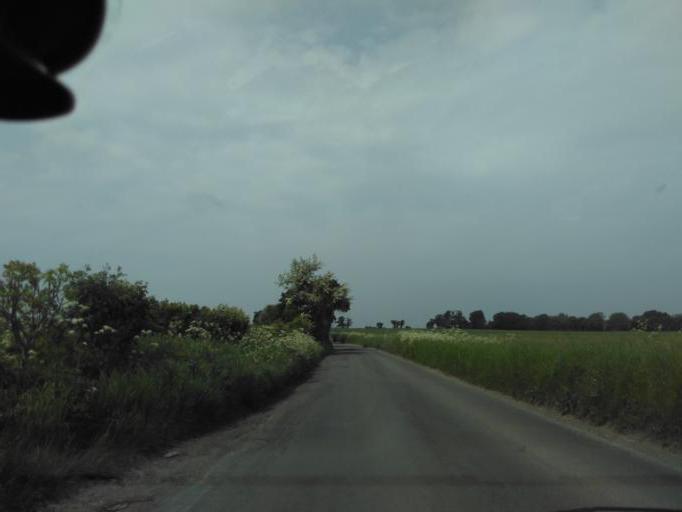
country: GB
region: England
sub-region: Kent
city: Canterbury
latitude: 51.2389
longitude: 1.0708
